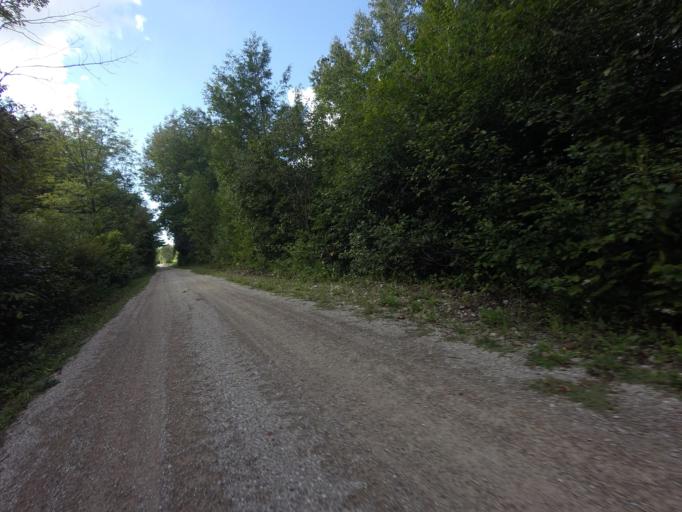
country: CA
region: Ontario
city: Huron East
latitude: 43.7399
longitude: -81.4724
